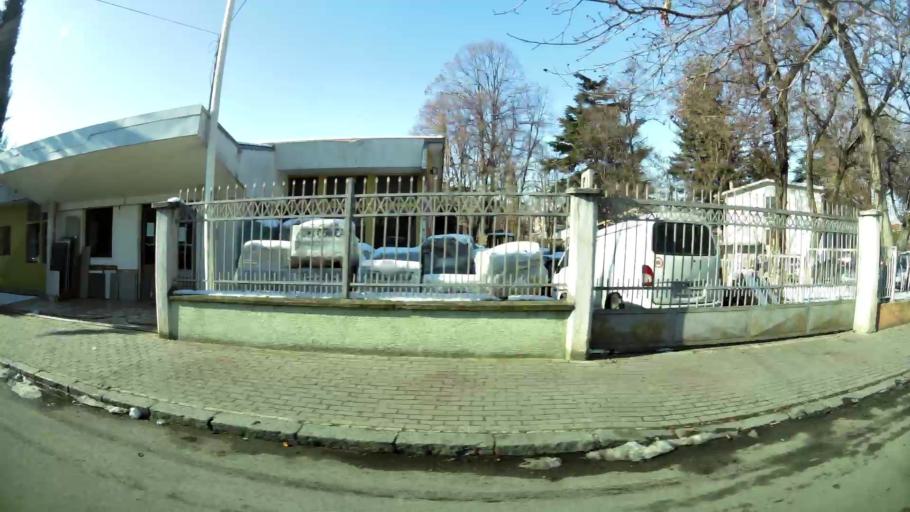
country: MK
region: Saraj
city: Saraj
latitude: 42.0055
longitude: 21.3503
